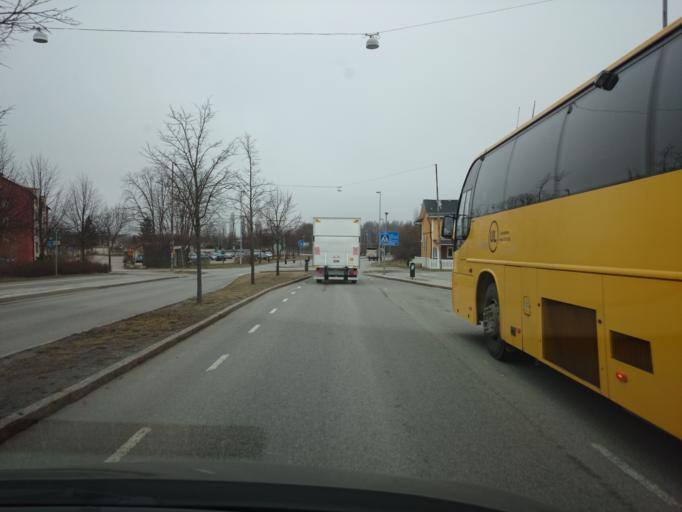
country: SE
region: Uppsala
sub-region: Uppsala Kommun
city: Gamla Uppsala
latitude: 59.8787
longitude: 17.6229
